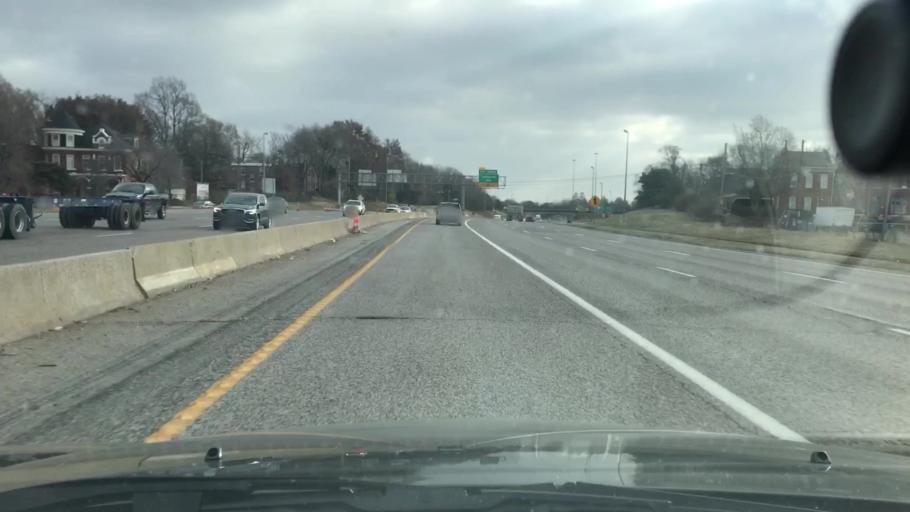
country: US
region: Missouri
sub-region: City of Saint Louis
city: St. Louis
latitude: 38.6136
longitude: -90.2206
